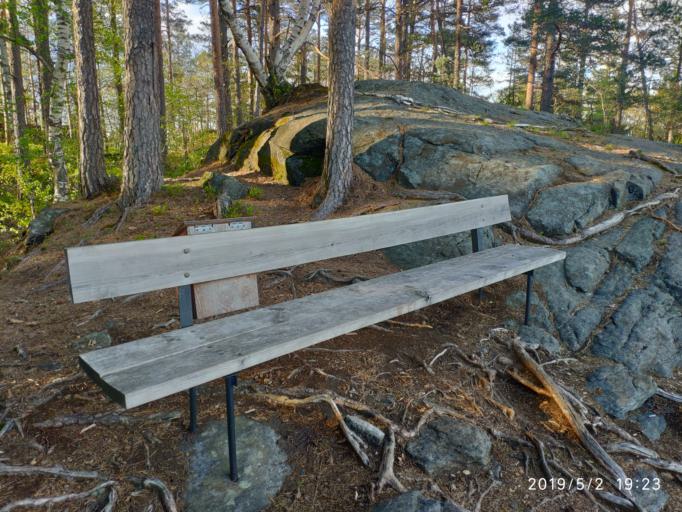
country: NO
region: Telemark
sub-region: Kragero
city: Kragero
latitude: 58.8959
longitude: 9.4139
